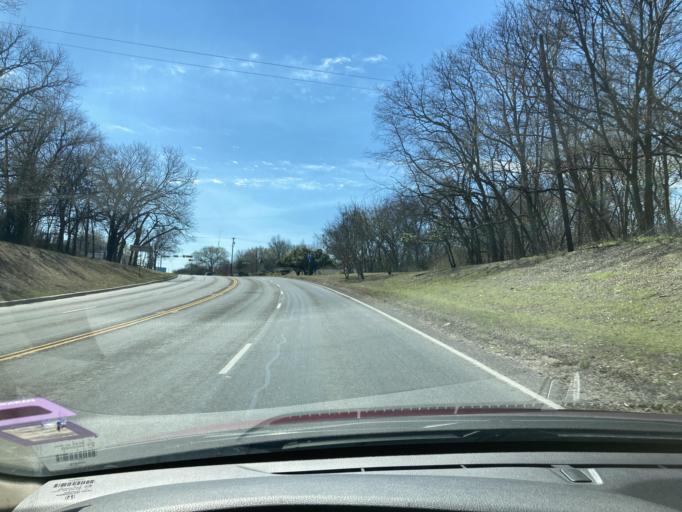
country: US
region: Texas
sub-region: Navarro County
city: Corsicana
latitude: 32.1015
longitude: -96.4638
